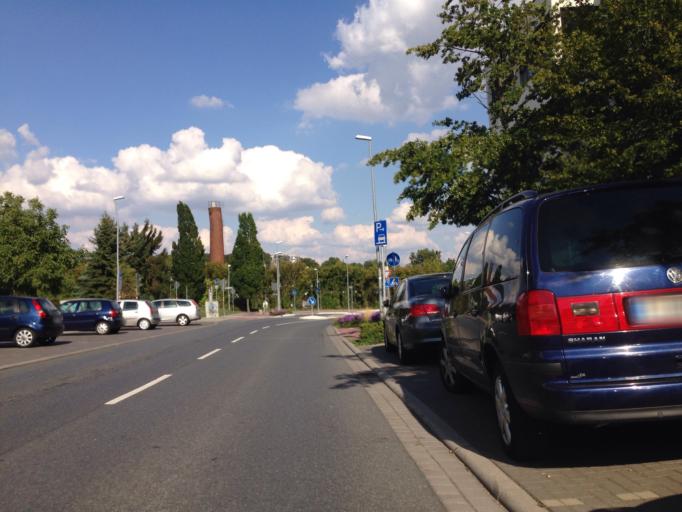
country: DE
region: Hesse
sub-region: Regierungsbezirk Darmstadt
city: Friedrichsdorf
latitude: 50.2557
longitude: 8.6422
